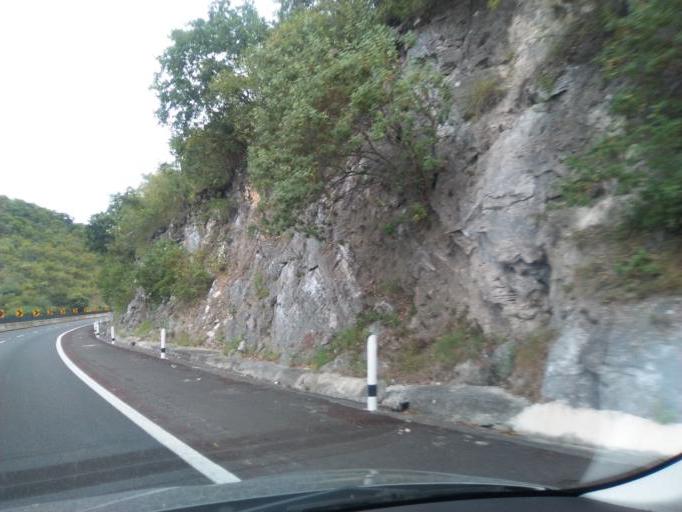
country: MX
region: Guerrero
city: Huitziltepec
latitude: 17.7133
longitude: -99.5093
